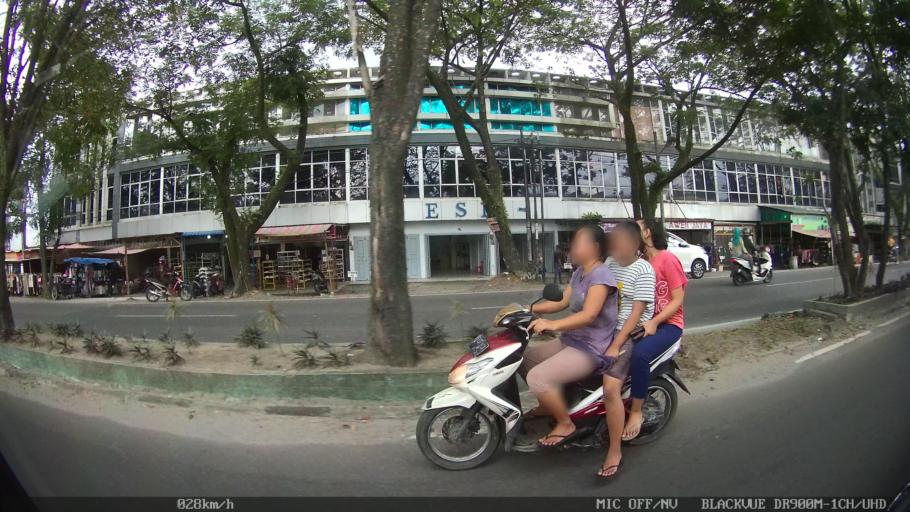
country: ID
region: North Sumatra
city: Sunggal
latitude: 3.5449
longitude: 98.6054
